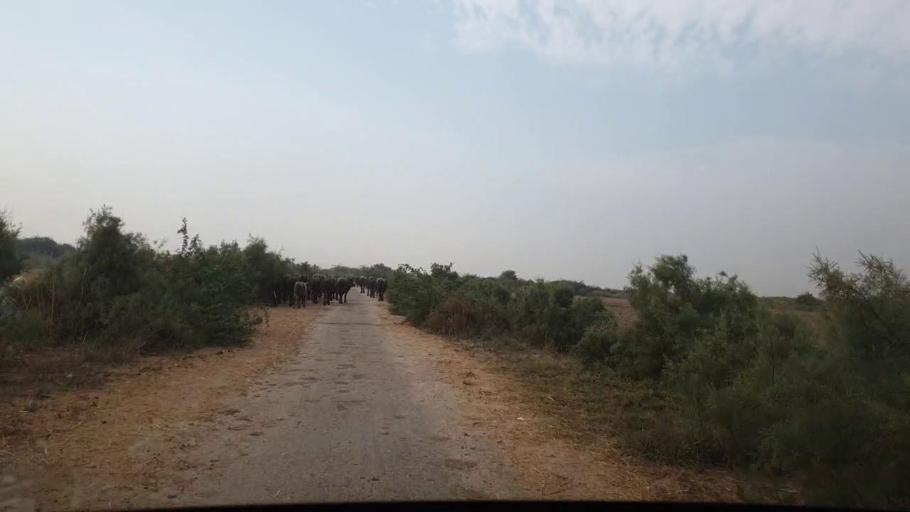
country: PK
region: Sindh
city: Chuhar Jamali
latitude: 24.4075
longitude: 67.9376
